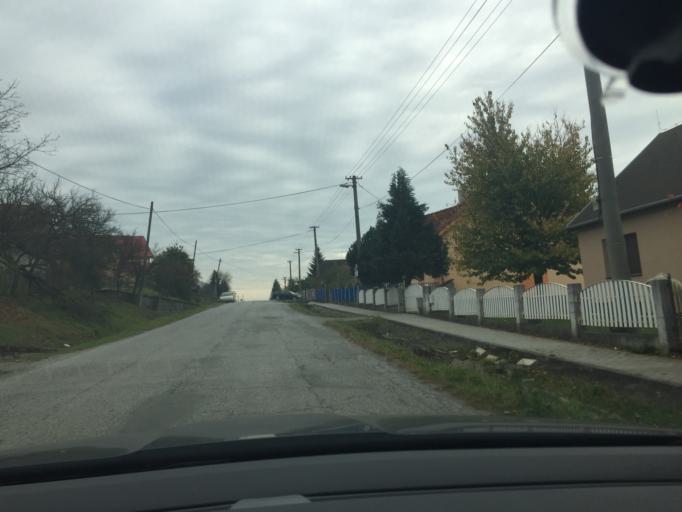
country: SK
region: Kosicky
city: Kosice
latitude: 48.8299
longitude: 21.3170
